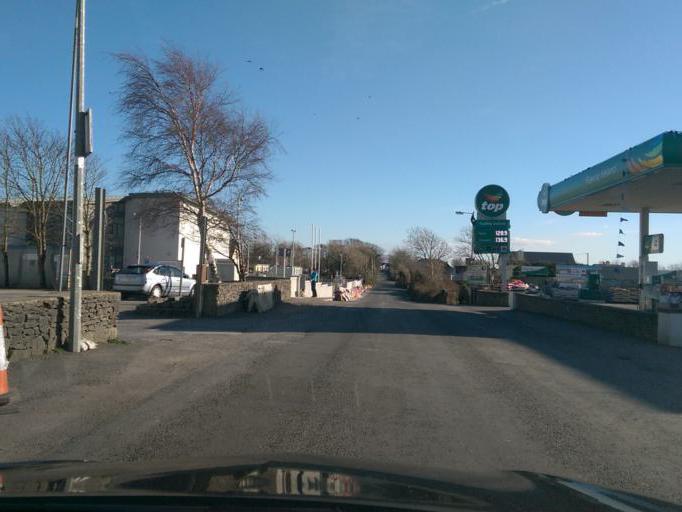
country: IE
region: Connaught
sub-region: County Galway
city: Oranmore
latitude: 53.2322
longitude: -8.9502
